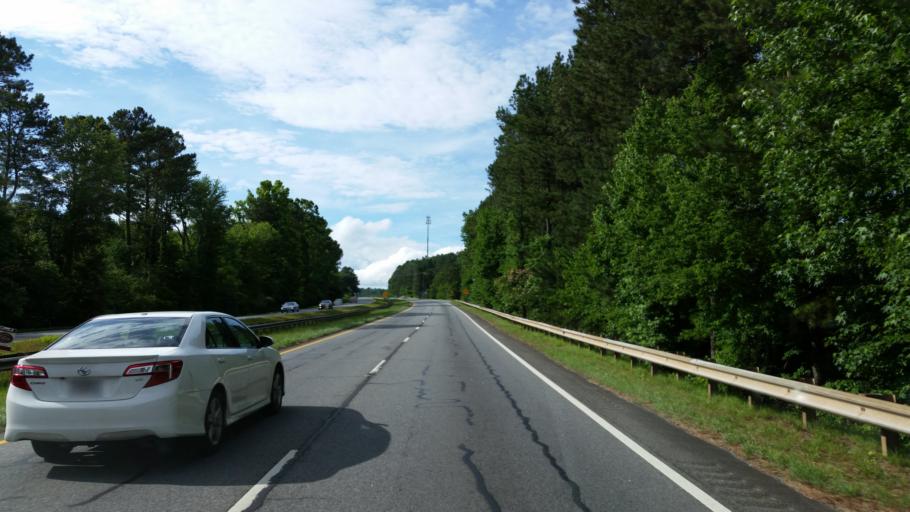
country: US
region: Georgia
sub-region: Bartow County
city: Emerson
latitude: 34.1182
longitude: -84.7489
